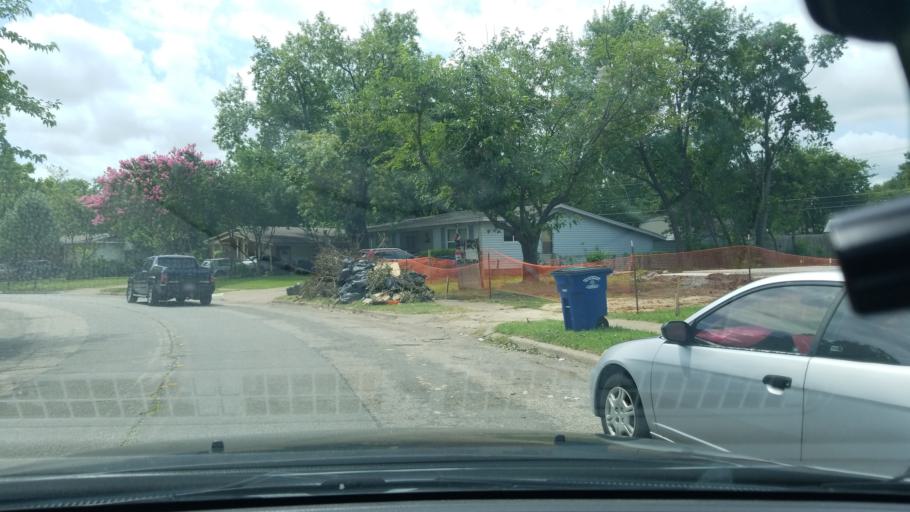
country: US
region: Texas
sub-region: Dallas County
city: Mesquite
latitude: 32.8209
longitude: -96.6745
